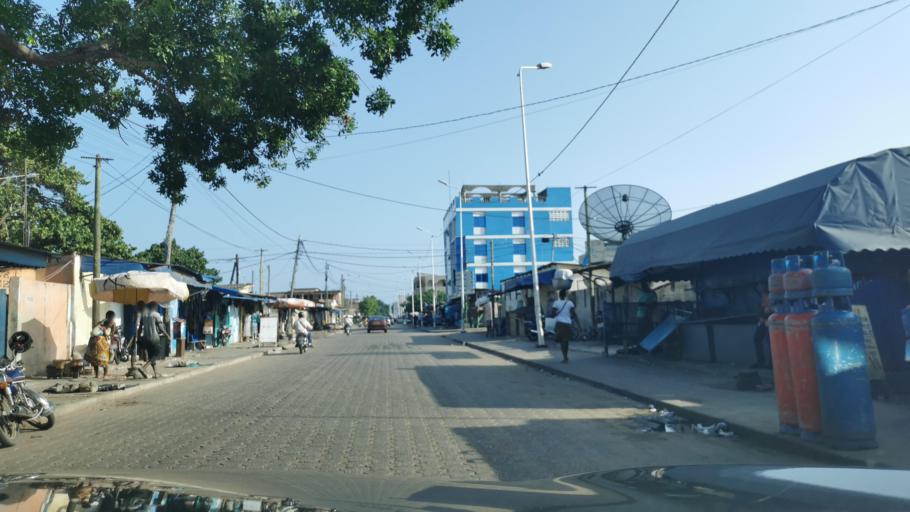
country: TG
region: Maritime
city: Lome
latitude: 6.1430
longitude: 1.2290
